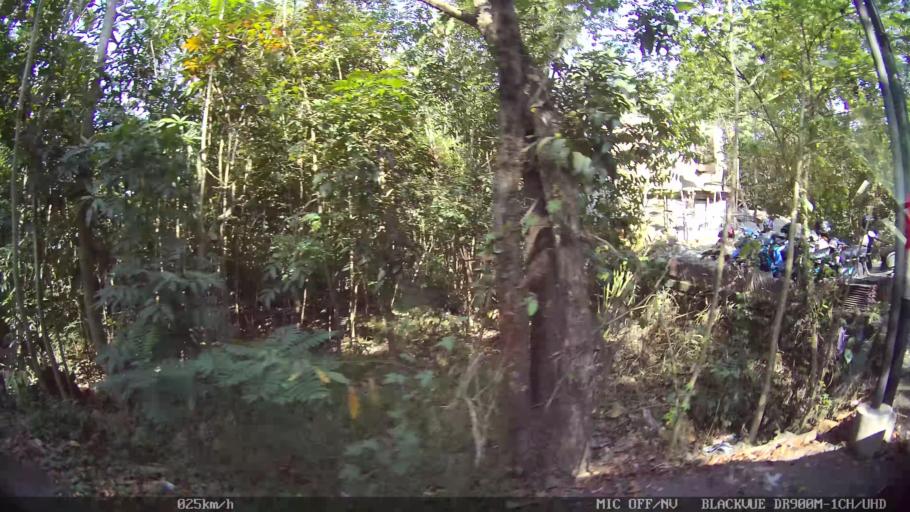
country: ID
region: Daerah Istimewa Yogyakarta
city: Kasihan
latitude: -7.8349
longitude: 110.3368
